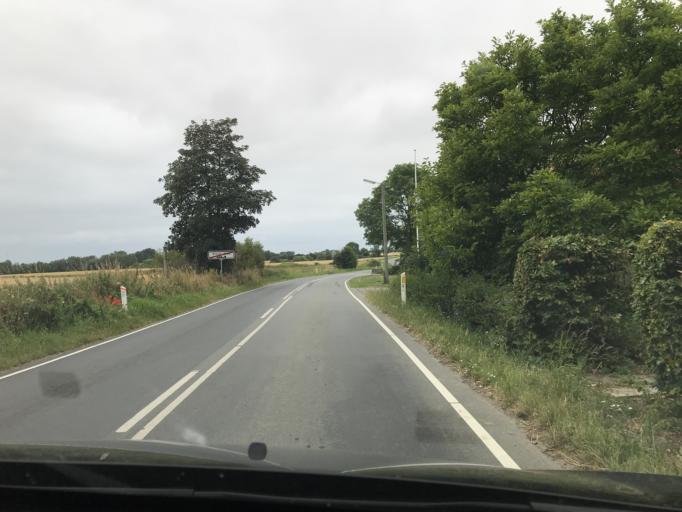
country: DK
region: South Denmark
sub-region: AEro Kommune
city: AEroskobing
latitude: 54.8564
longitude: 10.3979
